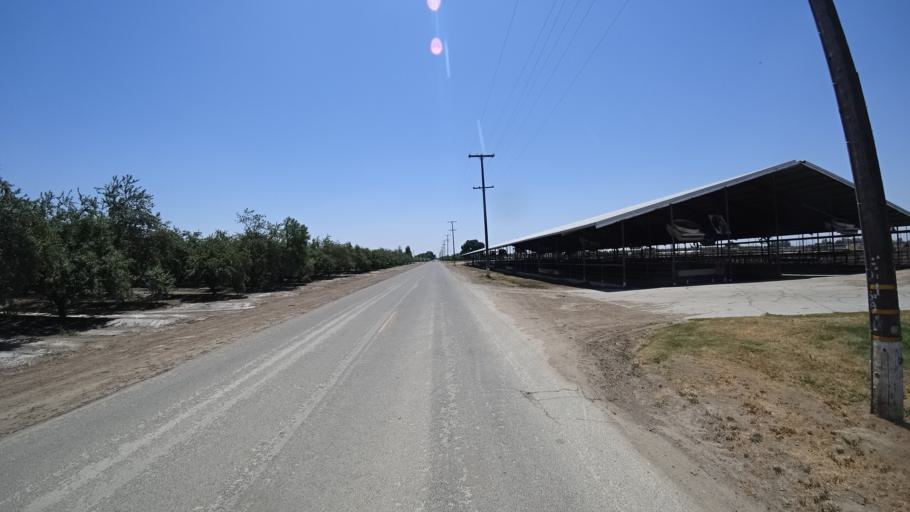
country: US
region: California
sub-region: Kings County
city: Armona
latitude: 36.3203
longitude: -119.7270
